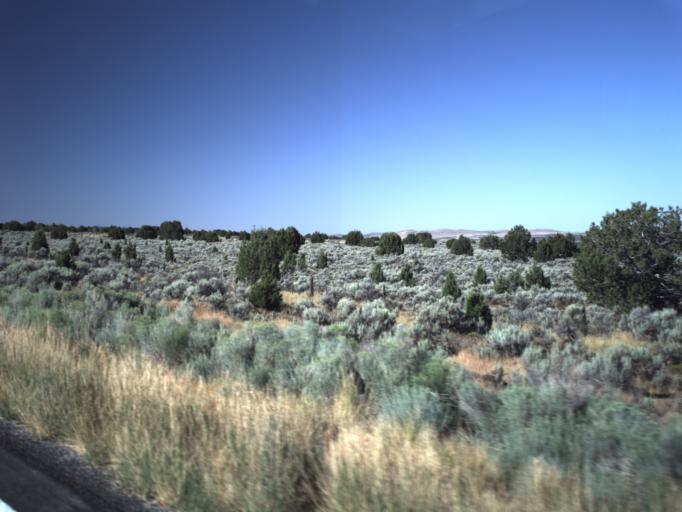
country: US
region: Utah
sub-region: Juab County
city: Mona
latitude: 39.8487
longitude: -112.1381
